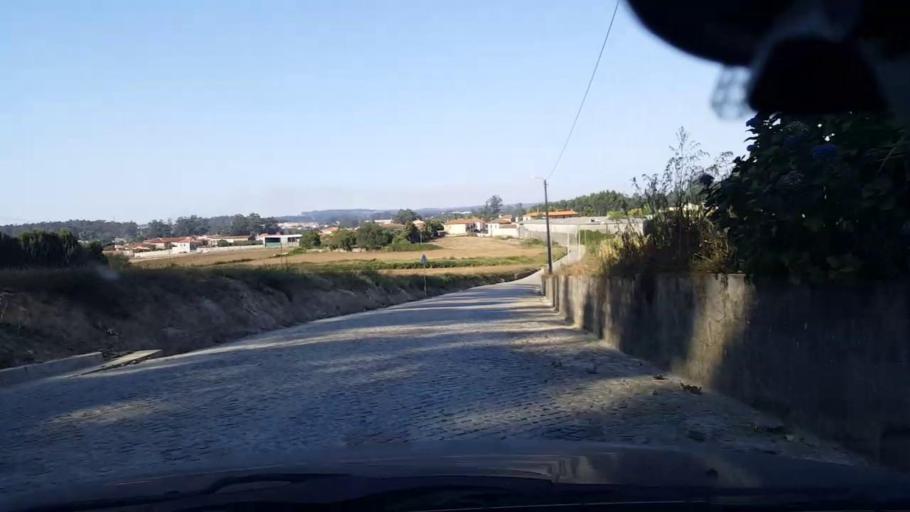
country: PT
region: Porto
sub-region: Vila do Conde
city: Arvore
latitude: 41.3536
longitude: -8.7189
